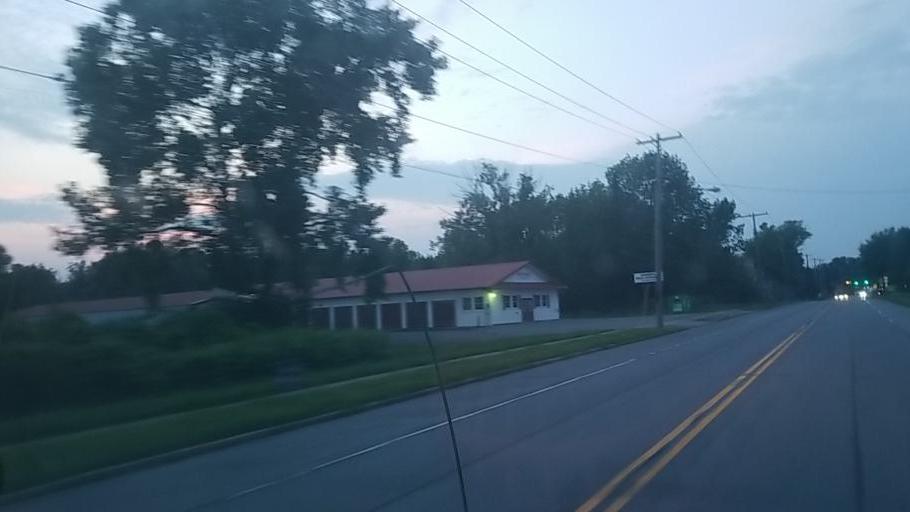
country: US
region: New York
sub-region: Fulton County
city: Johnstown
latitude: 43.0048
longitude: -74.3590
